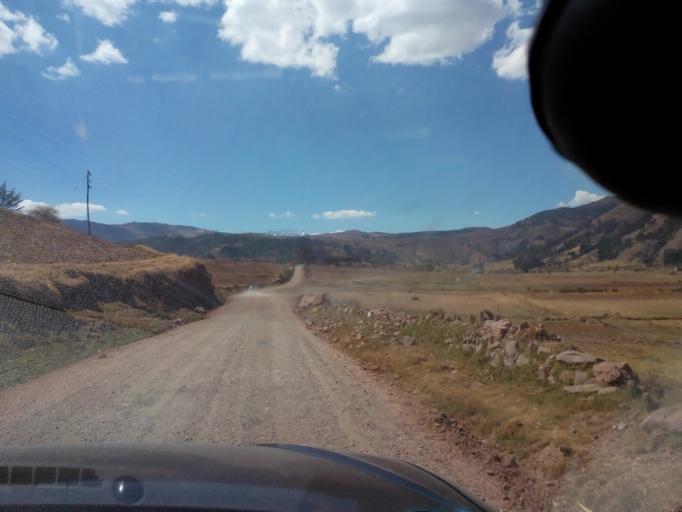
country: PE
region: Cusco
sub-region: Provincia de Anta
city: Huarocondo
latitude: -13.4248
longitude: -72.2153
